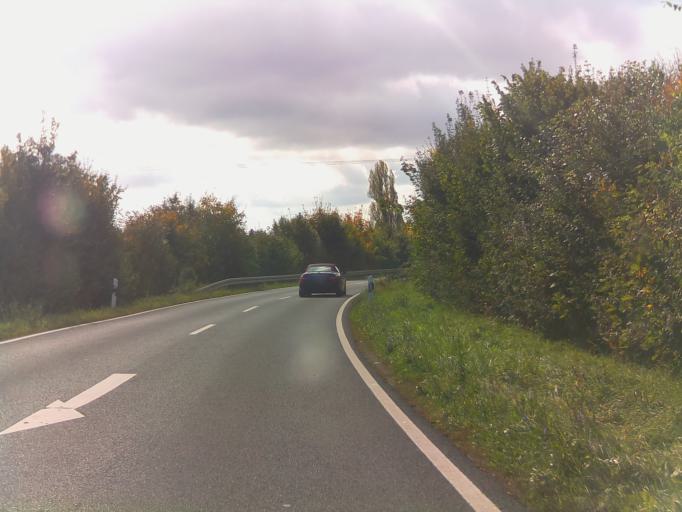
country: DE
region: Bavaria
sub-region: Regierungsbezirk Unterfranken
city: Frickenhausen
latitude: 49.7098
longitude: 10.0792
